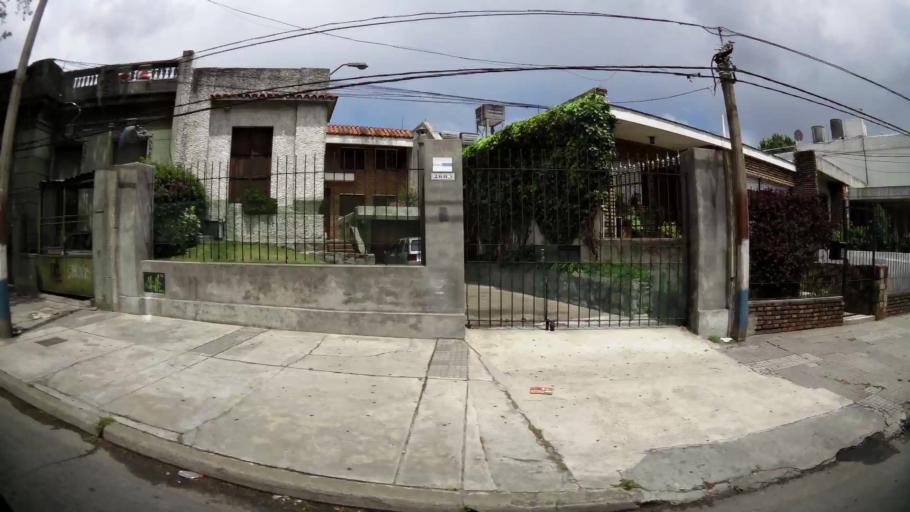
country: UY
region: Montevideo
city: Montevideo
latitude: -34.8803
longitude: -56.1546
